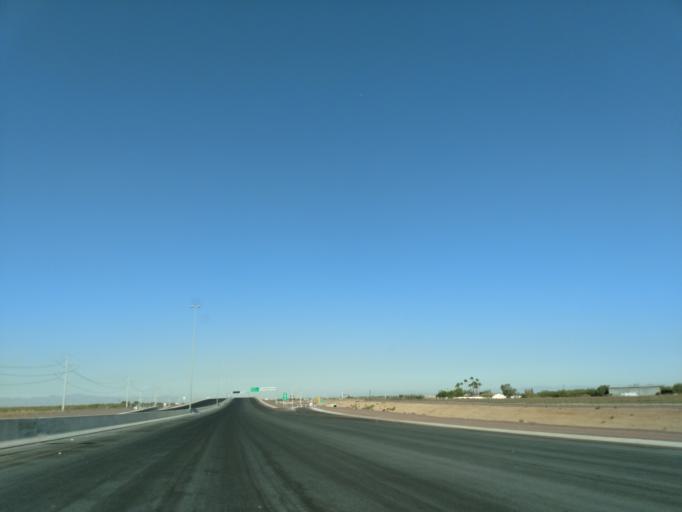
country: US
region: Arizona
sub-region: Maricopa County
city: Laveen
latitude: 33.3295
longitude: -112.1719
